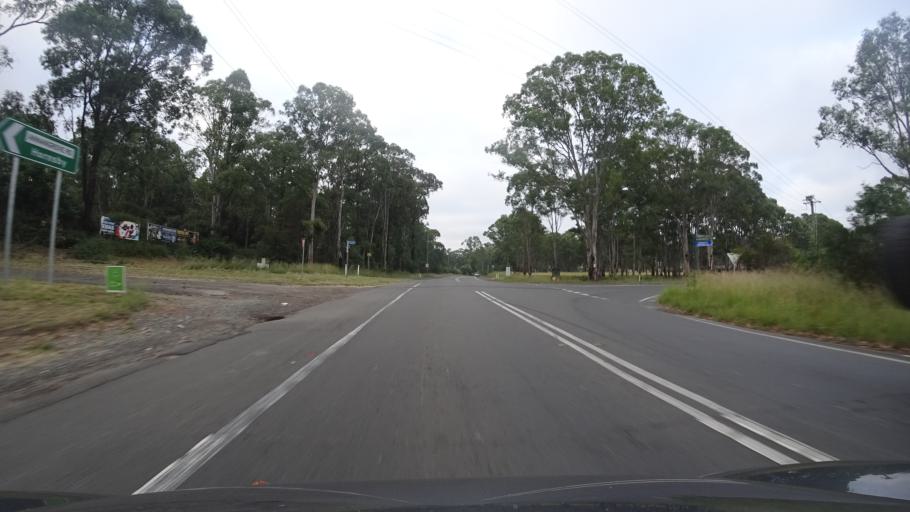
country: AU
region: New South Wales
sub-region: Blacktown
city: Rouse Hill
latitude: -33.6608
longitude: 150.9238
